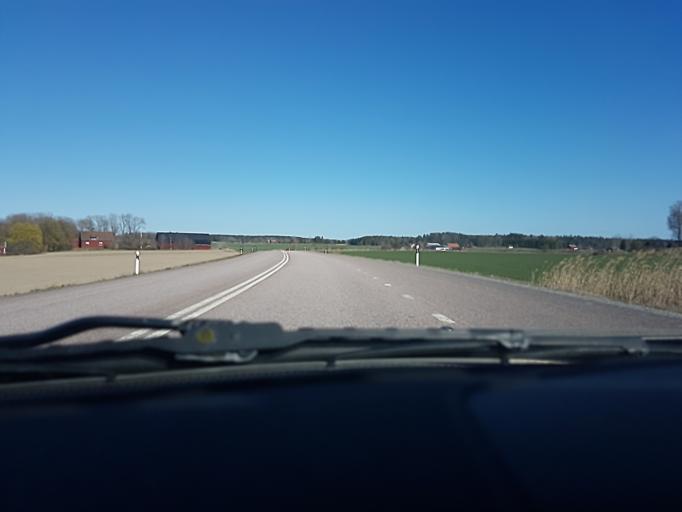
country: SE
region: Uppsala
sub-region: Enkopings Kommun
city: Hummelsta
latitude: 59.6203
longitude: 16.8695
